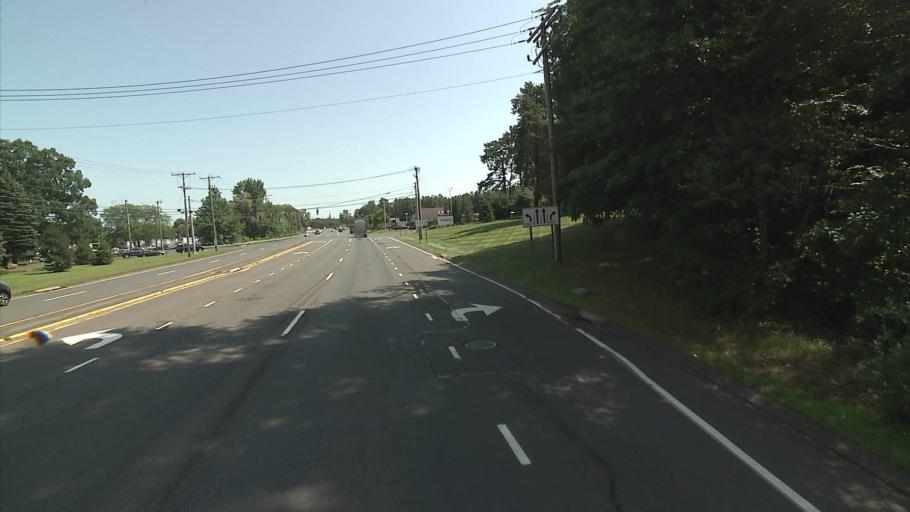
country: US
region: Connecticut
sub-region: Hartford County
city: Tariffville
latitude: 41.9298
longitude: -72.7103
